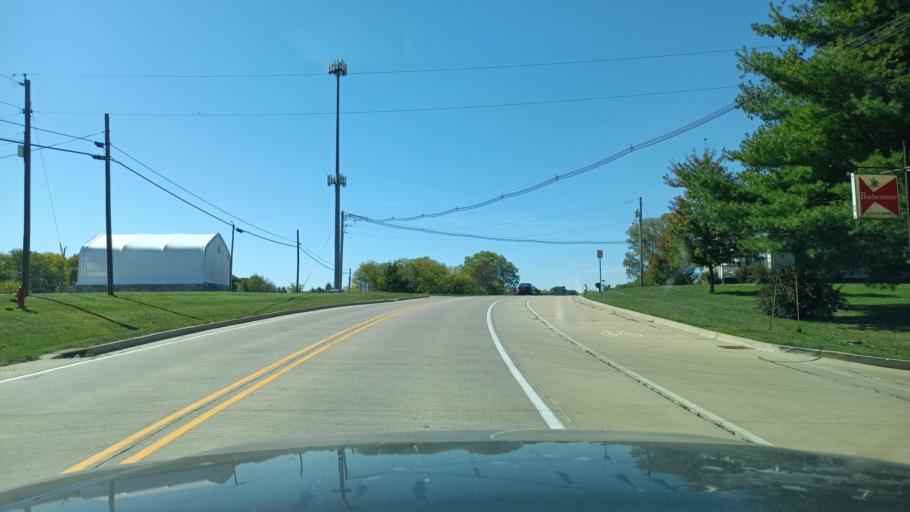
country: US
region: Illinois
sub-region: Champaign County
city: Mahomet
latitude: 40.1946
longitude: -88.3853
